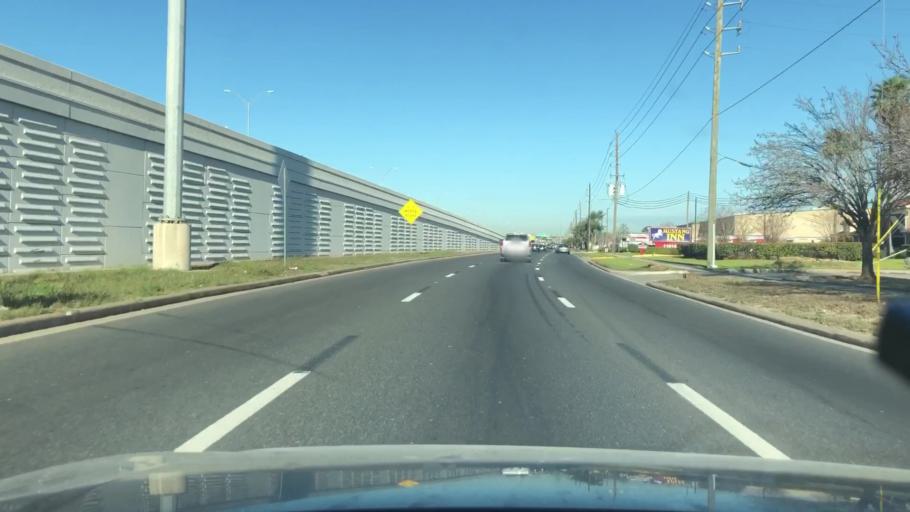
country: US
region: Texas
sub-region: Fort Bend County
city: Missouri City
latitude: 29.6460
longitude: -95.5407
